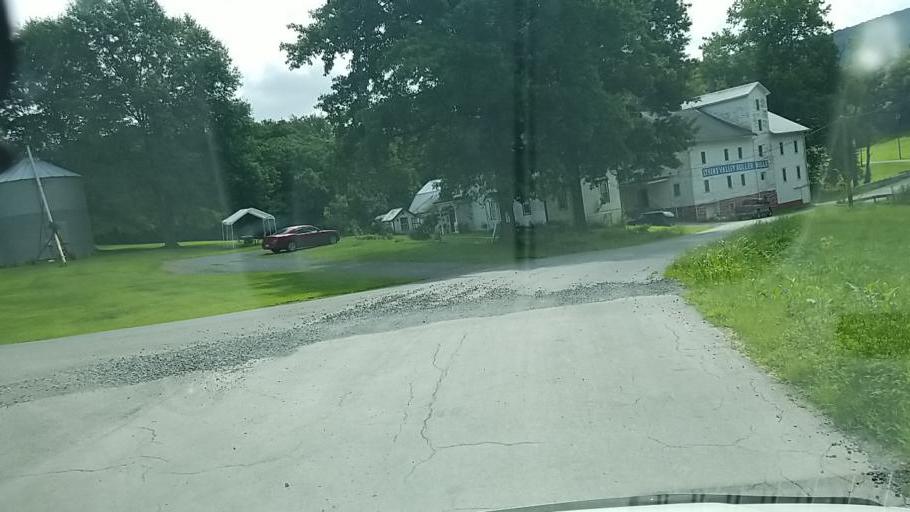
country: US
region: Pennsylvania
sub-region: Dauphin County
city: Elizabethville
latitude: 40.5458
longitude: -76.8689
